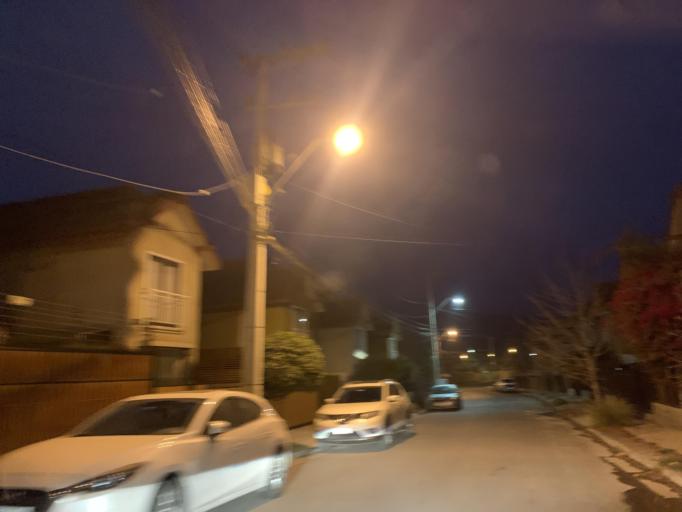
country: CL
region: Valparaiso
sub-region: Provincia de Marga Marga
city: Villa Alemana
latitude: -33.0584
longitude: -71.3374
